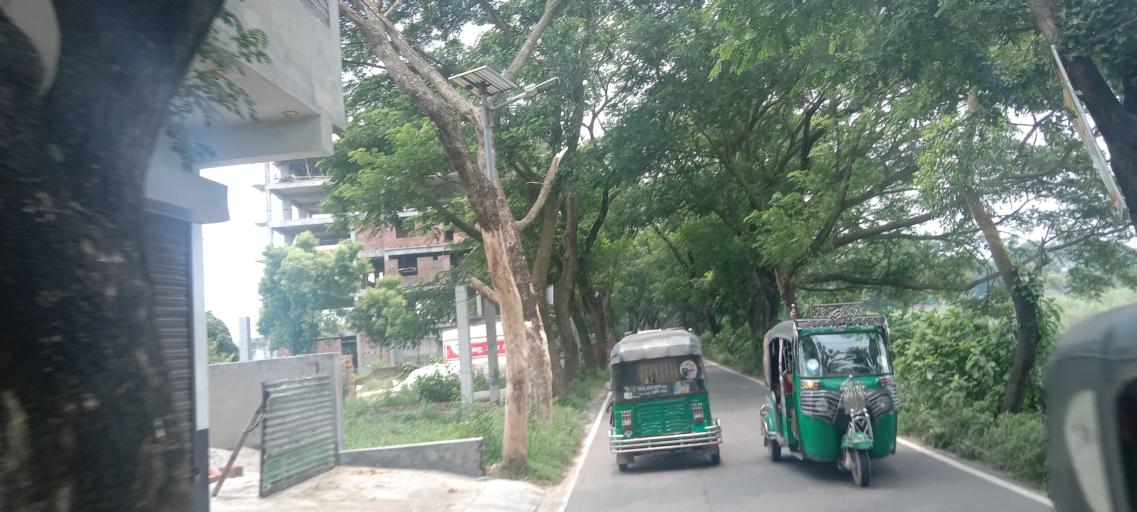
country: BD
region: Dhaka
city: Azimpur
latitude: 23.7147
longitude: 90.3447
